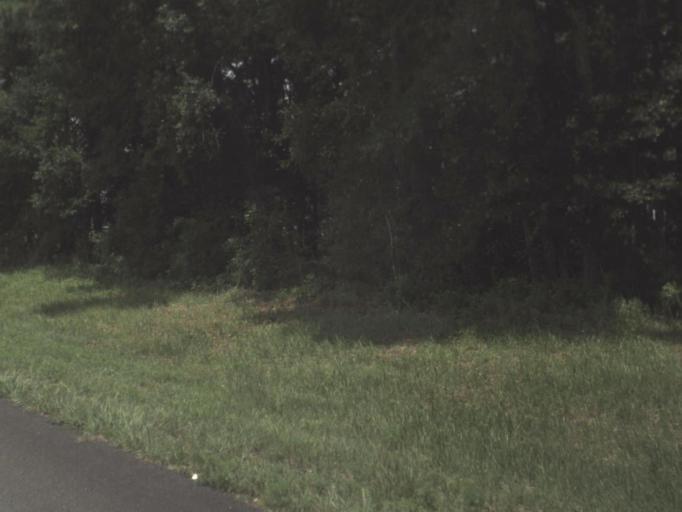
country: US
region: Florida
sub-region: Levy County
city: Williston
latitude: 29.4020
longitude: -82.4505
